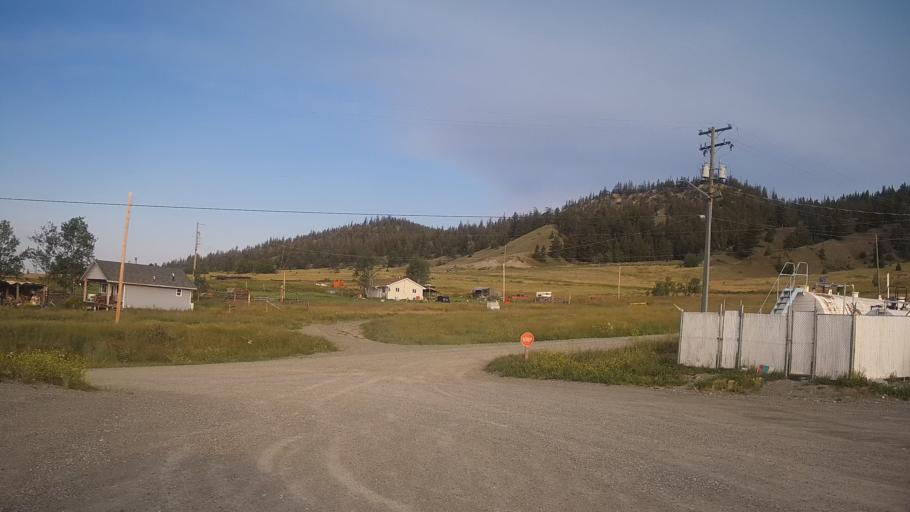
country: CA
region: British Columbia
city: Hanceville
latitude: 52.1407
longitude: -123.9529
